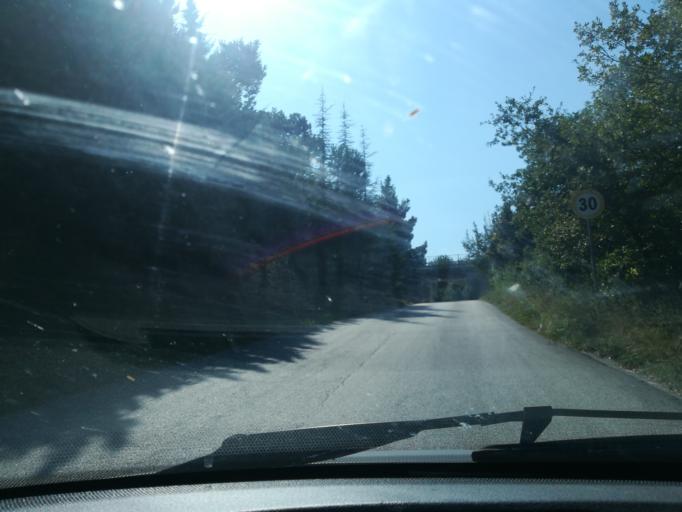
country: IT
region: The Marches
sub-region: Provincia di Macerata
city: Caldarola
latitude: 43.1515
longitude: 13.2245
